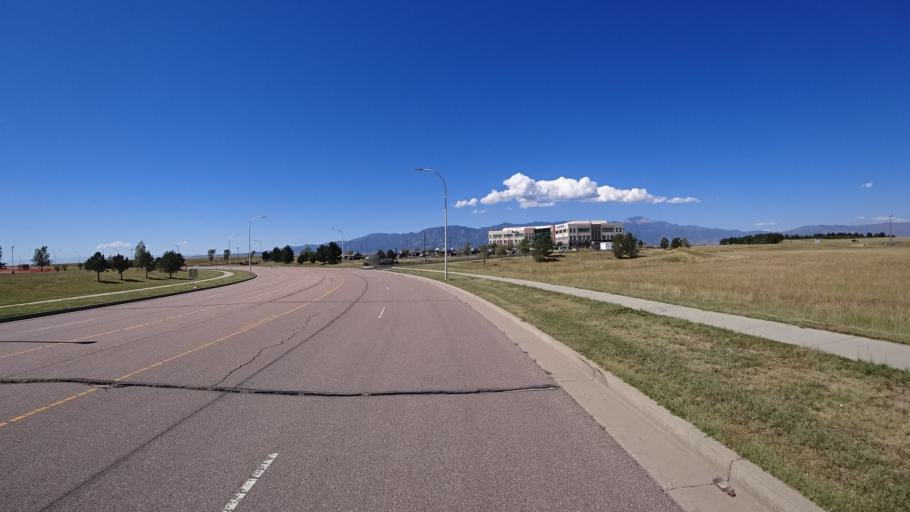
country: US
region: Colorado
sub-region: El Paso County
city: Security-Widefield
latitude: 38.7794
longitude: -104.6988
